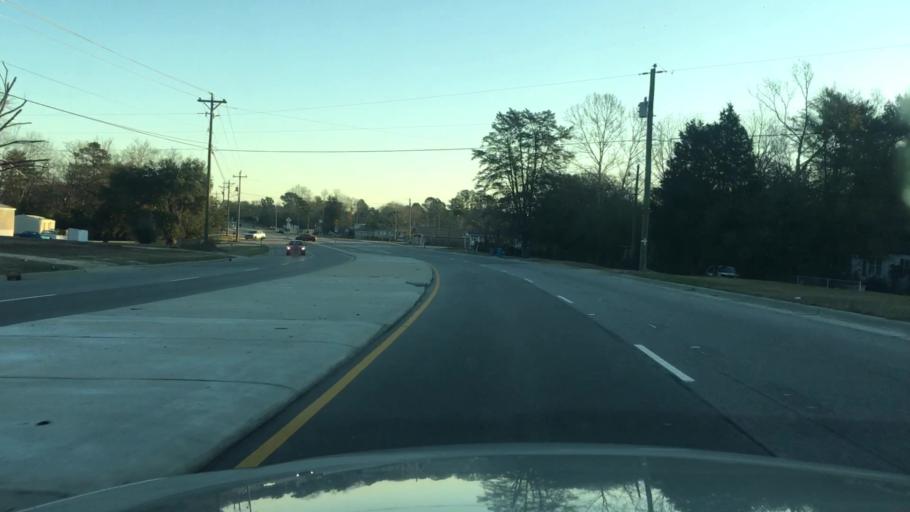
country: US
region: North Carolina
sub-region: Cumberland County
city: Hope Mills
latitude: 34.9986
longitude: -78.9318
